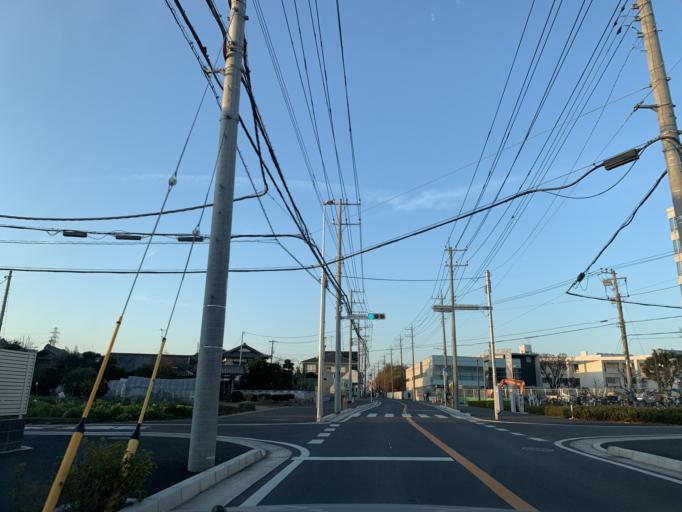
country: JP
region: Chiba
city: Kashiwa
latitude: 35.8750
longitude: 139.9383
